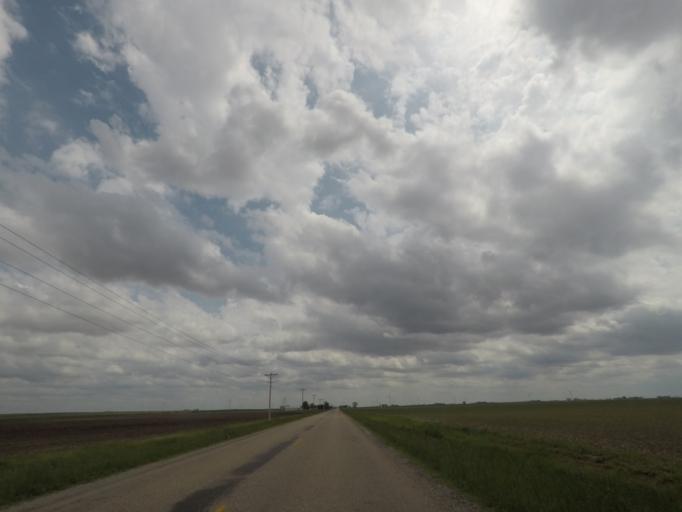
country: US
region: Illinois
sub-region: Macon County
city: Maroa
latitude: 40.0812
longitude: -89.0859
